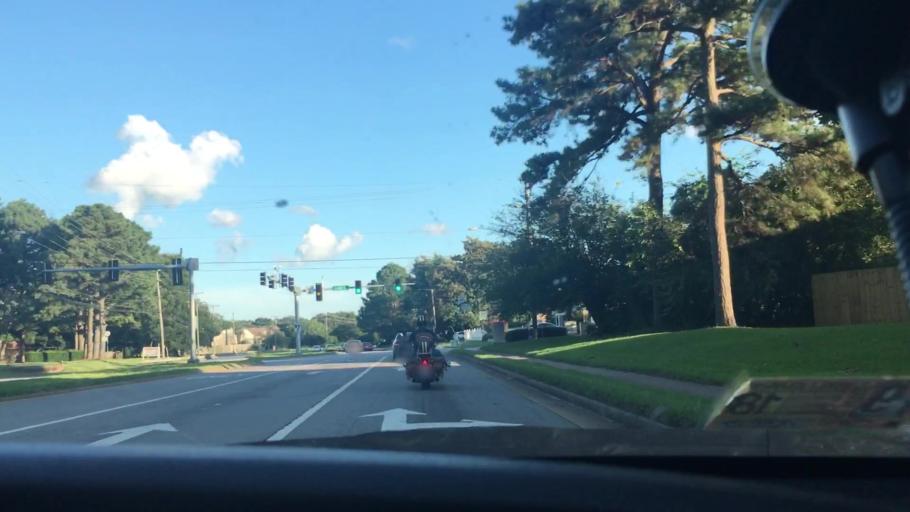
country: US
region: Virginia
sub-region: City of Chesapeake
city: Chesapeake
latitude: 36.8846
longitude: -76.1349
